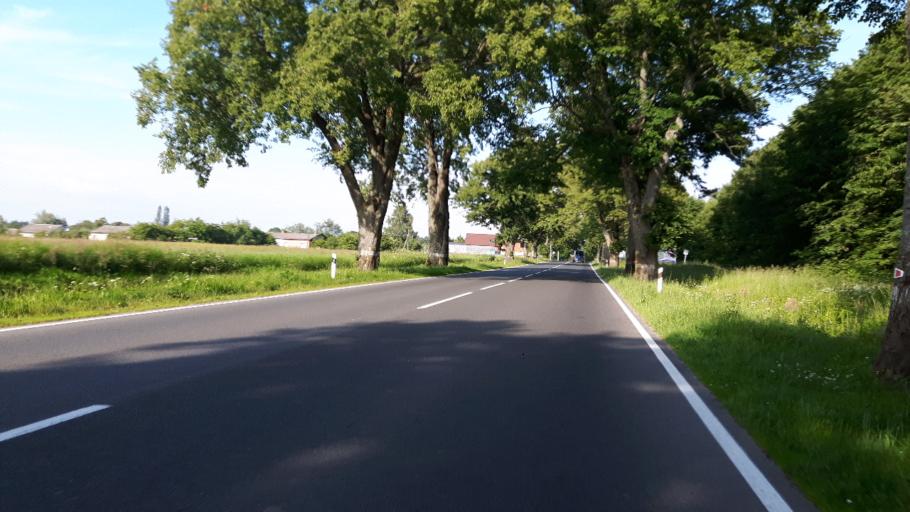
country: RU
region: Kaliningrad
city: Ladushkin
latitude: 54.4998
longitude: 20.0873
